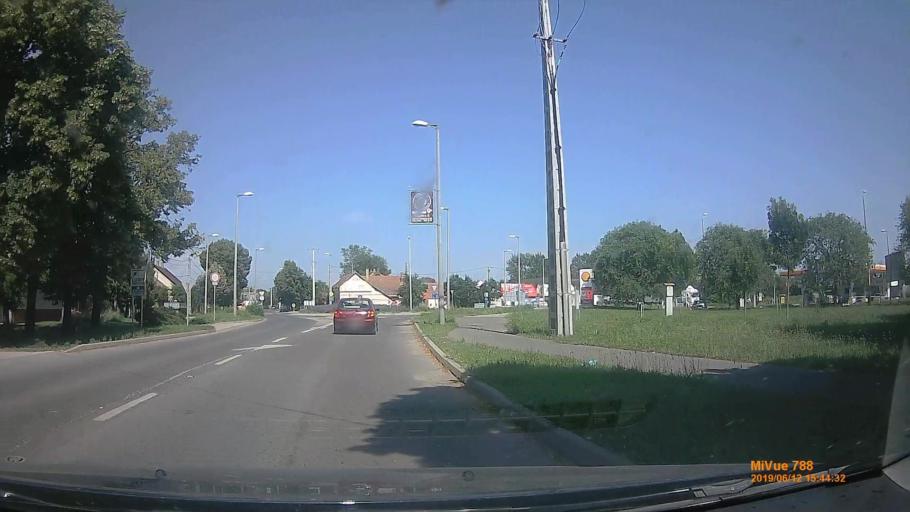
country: HU
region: Csongrad
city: Mako
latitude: 46.2169
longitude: 20.5010
